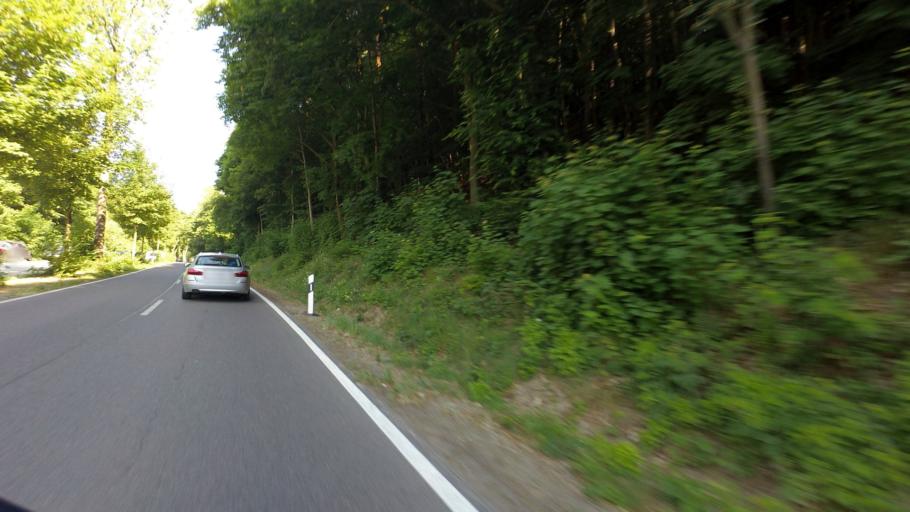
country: DE
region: Saxony
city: Bad Schandau
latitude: 50.9011
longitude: 14.2180
